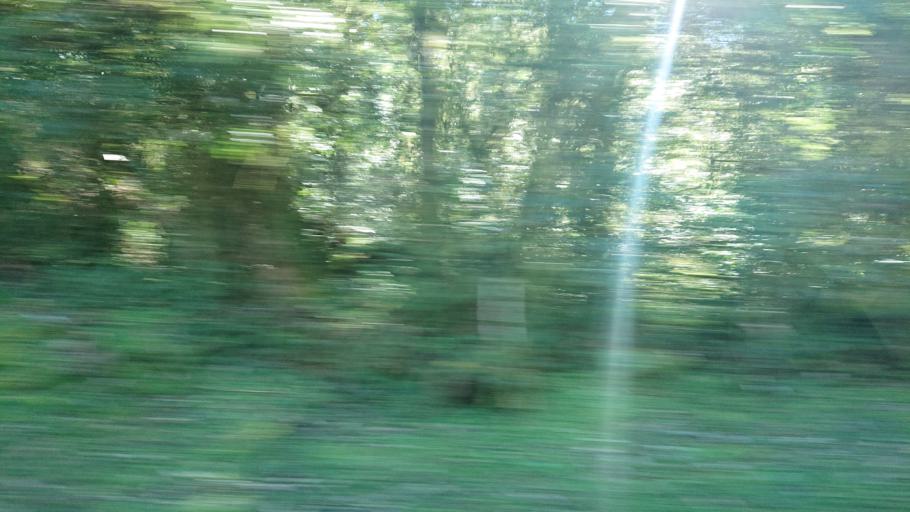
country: TW
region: Taiwan
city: Daxi
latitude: 24.4021
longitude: 121.3633
